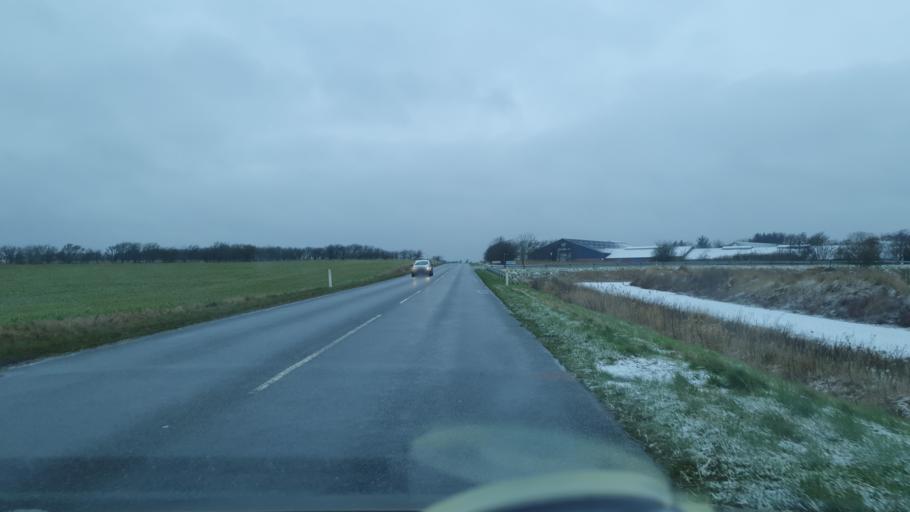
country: DK
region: North Denmark
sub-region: Jammerbugt Kommune
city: Brovst
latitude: 57.1218
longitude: 9.4928
